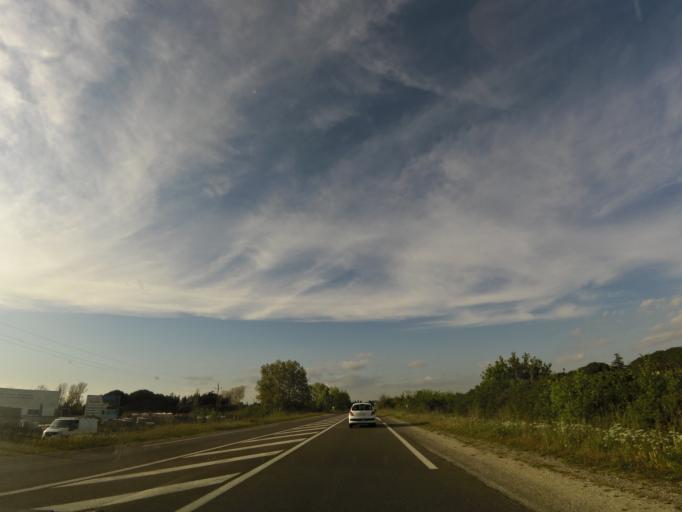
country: FR
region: Languedoc-Roussillon
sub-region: Departement de l'Herault
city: Saint-Just
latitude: 43.6533
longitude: 4.1388
